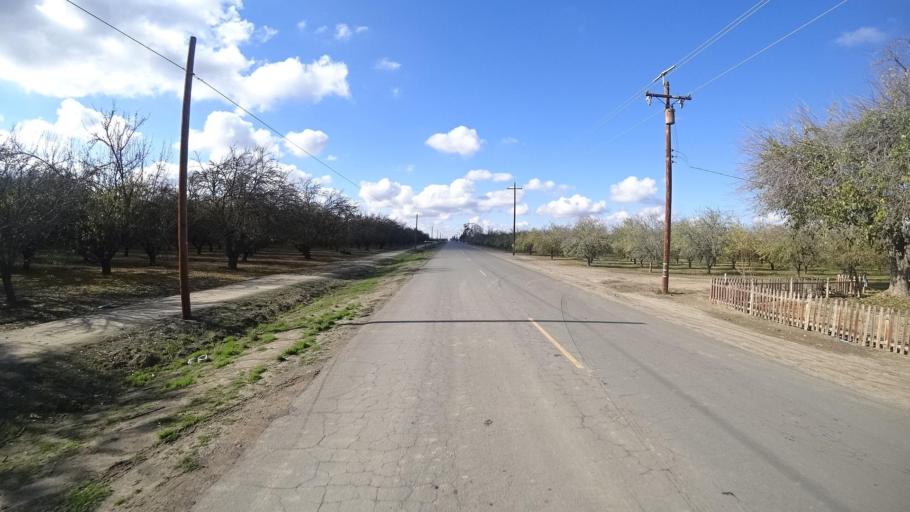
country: US
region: California
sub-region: Kern County
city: McFarland
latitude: 35.6888
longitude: -119.2641
